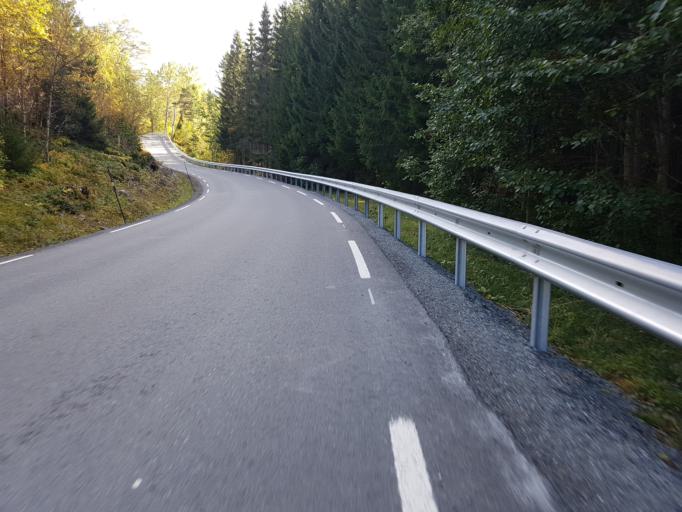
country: NO
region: Sor-Trondelag
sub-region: Malvik
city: Malvik
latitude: 63.3691
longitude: 10.6165
